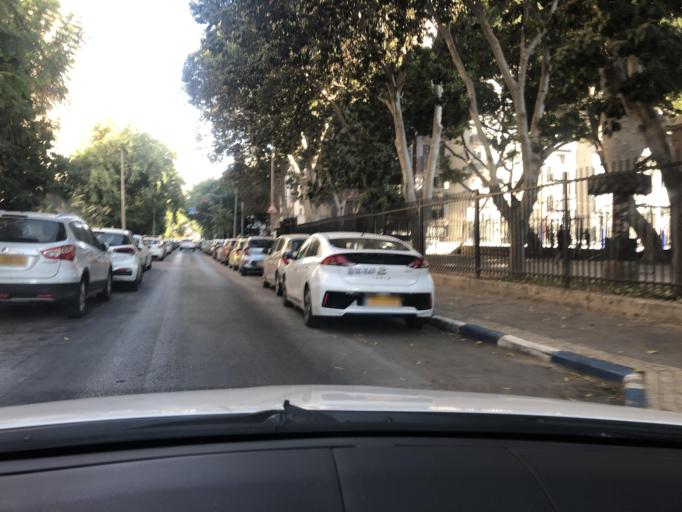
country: IL
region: Tel Aviv
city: Giv`atayim
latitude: 32.0613
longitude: 34.8254
